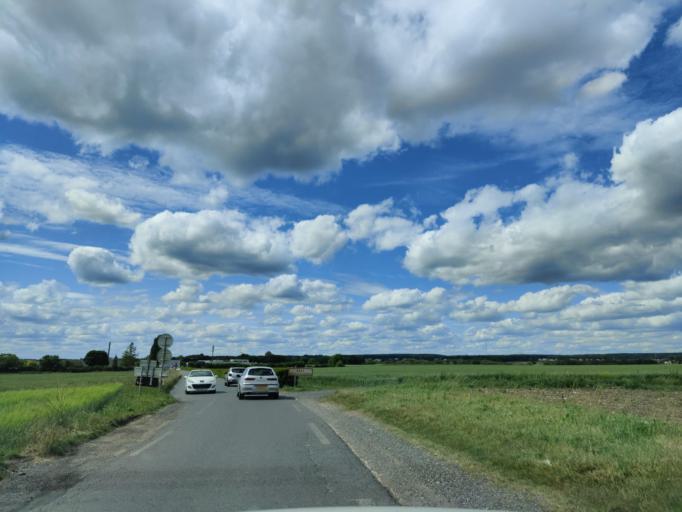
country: FR
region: Ile-de-France
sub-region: Departement de l'Essonne
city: Egly
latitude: 48.5697
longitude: 2.2126
